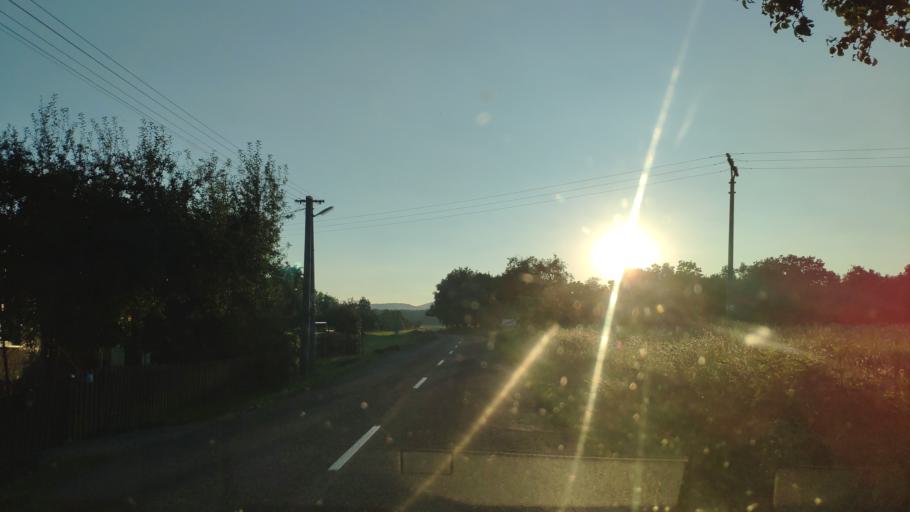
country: SK
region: Kosicky
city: Secovce
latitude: 48.7370
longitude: 21.6117
